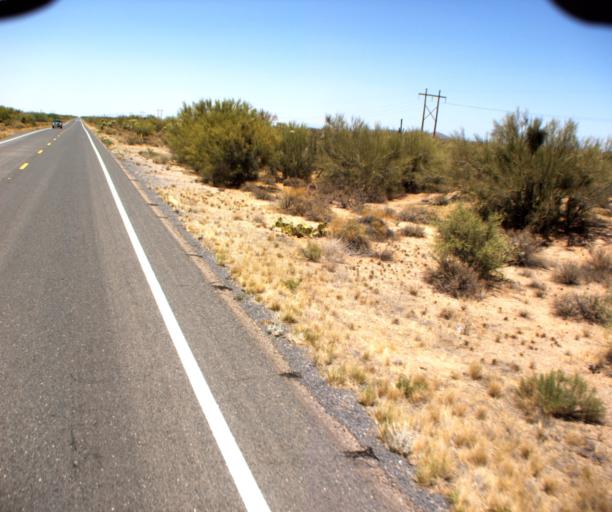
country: US
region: Arizona
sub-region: Pinal County
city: Florence
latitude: 32.8118
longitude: -111.1937
